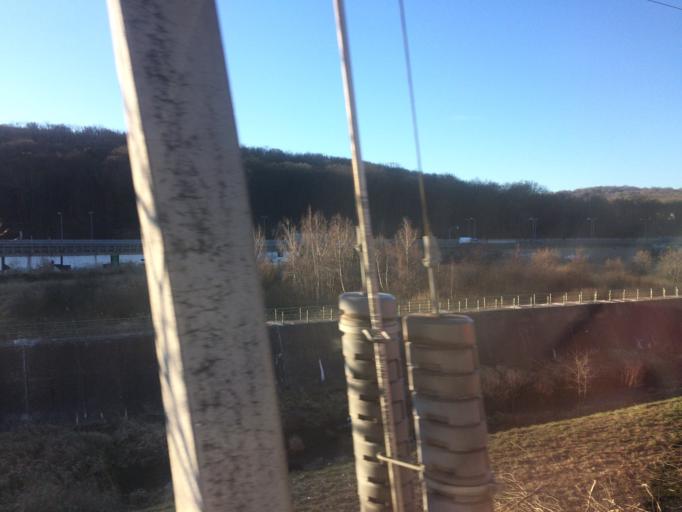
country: AT
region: Lower Austria
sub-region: Politischer Bezirk Wien-Umgebung
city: Purkersdorf
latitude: 48.2020
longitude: 16.2449
